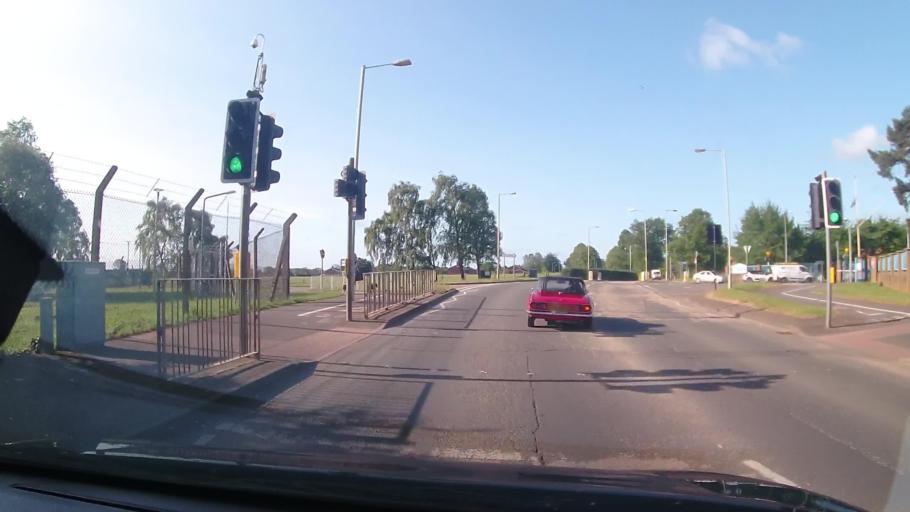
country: GB
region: England
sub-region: Shropshire
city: Shawbury
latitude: 52.7931
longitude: -2.6559
